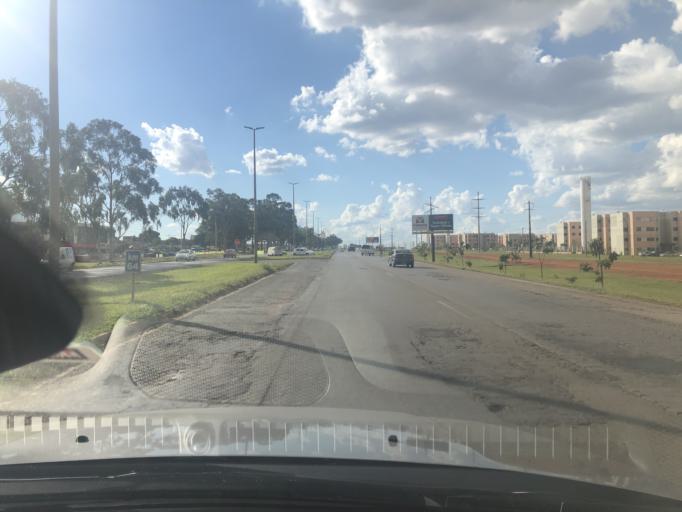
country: BR
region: Federal District
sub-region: Brasilia
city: Brasilia
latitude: -15.9172
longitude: -48.0489
